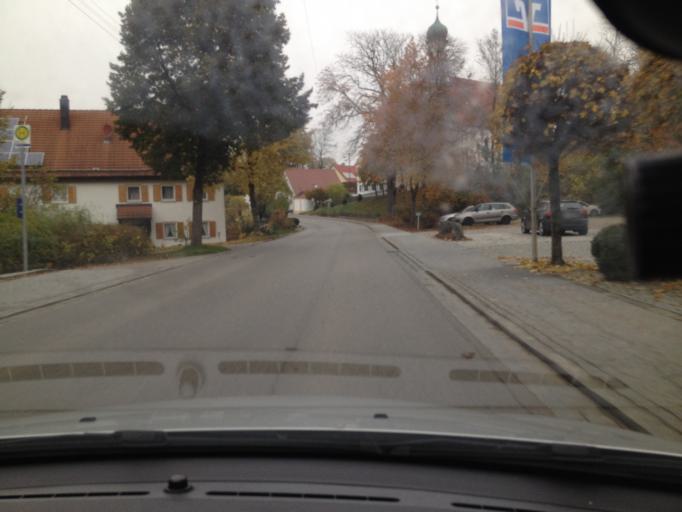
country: DE
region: Bavaria
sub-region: Swabia
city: Langerringen
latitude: 48.1486
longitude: 10.7567
